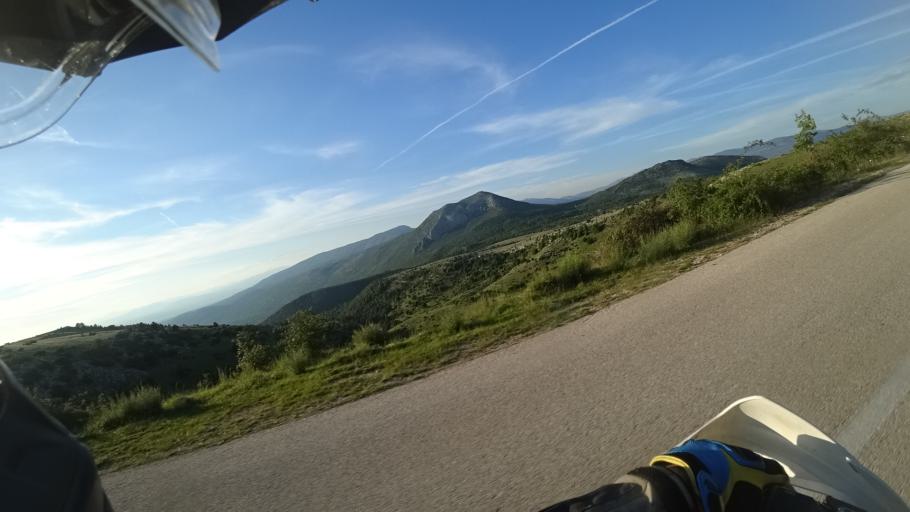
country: HR
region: Sibensko-Kniniska
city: Drnis
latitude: 43.8894
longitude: 16.3339
